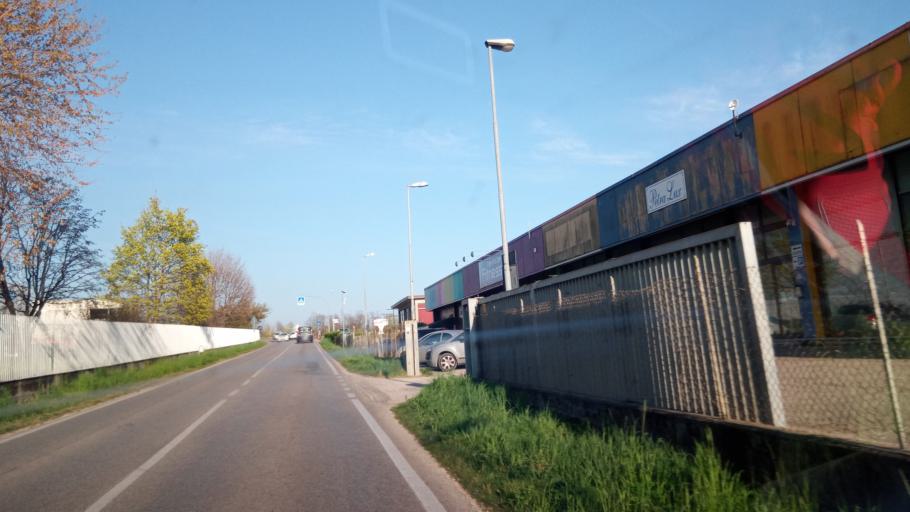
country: IT
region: Veneto
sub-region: Provincia di Treviso
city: Borso del Grappa
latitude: 45.8158
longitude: 11.8046
